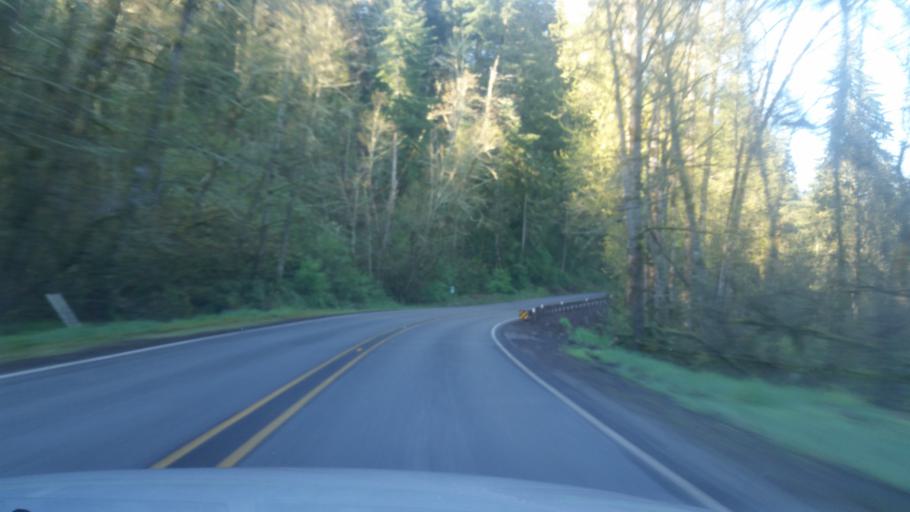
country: US
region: Washington
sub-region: Pierce County
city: Eatonville
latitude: 46.8581
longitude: -122.2543
